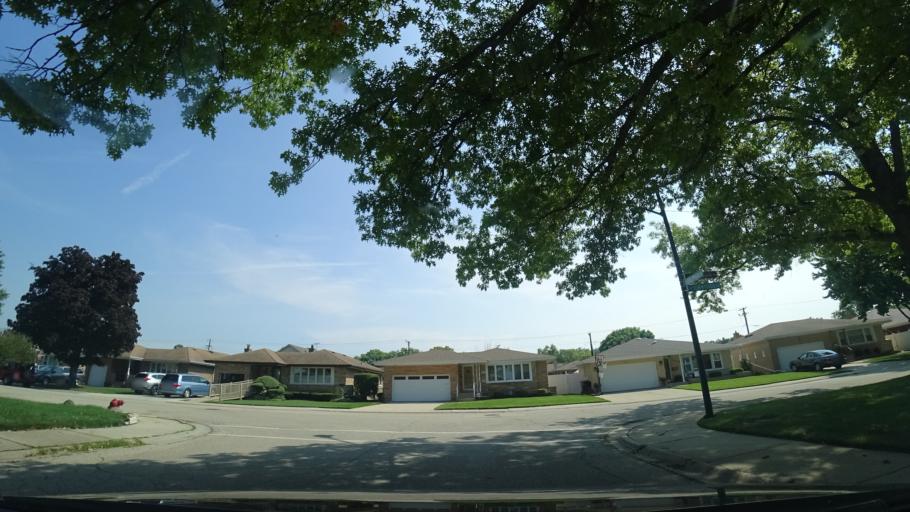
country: US
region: Illinois
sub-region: Cook County
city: Norridge
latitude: 41.9614
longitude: -87.8417
